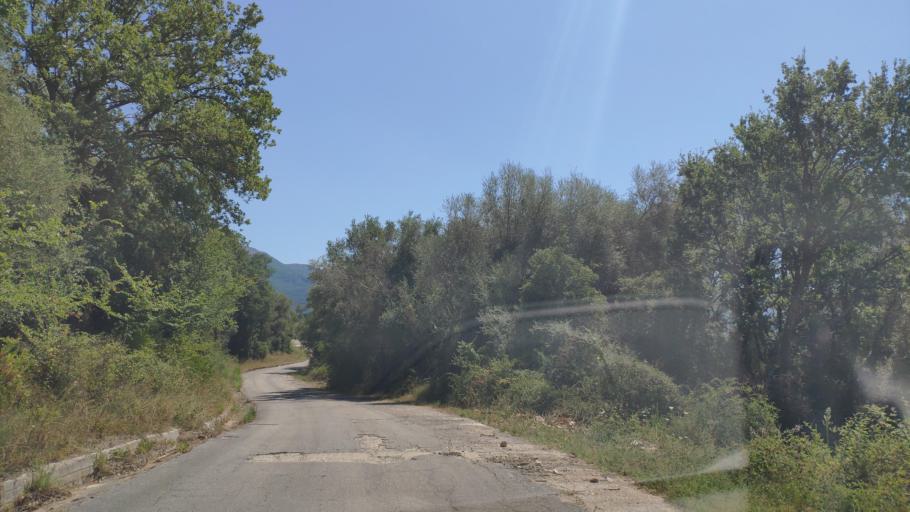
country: GR
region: Epirus
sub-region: Nomos Prevezis
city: Kanalaki
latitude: 39.2690
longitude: 20.6005
